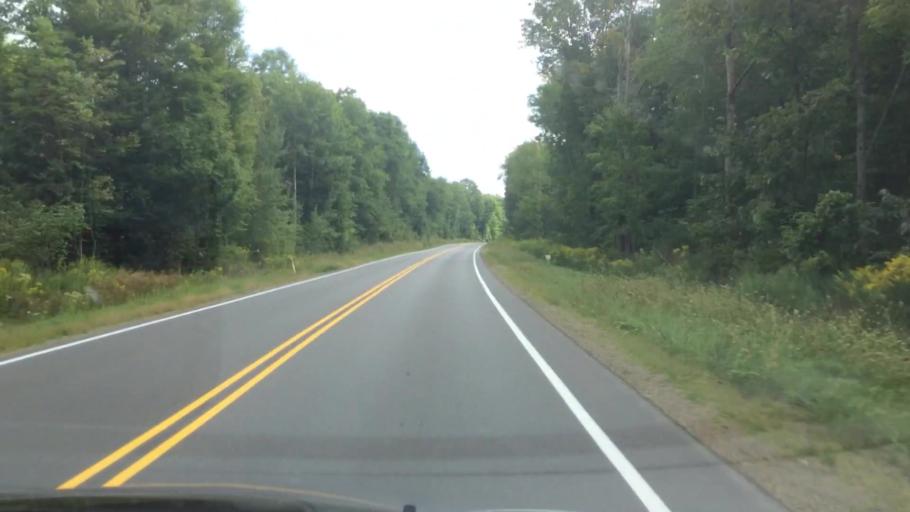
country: US
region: Pennsylvania
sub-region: McKean County
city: Bradford
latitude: 41.8846
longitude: -78.5845
